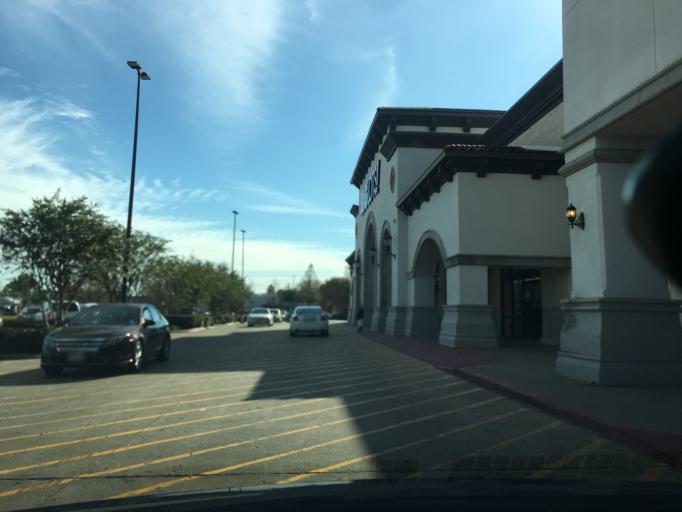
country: US
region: Texas
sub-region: Harris County
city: Cloverleaf
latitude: 29.8101
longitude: -95.1663
